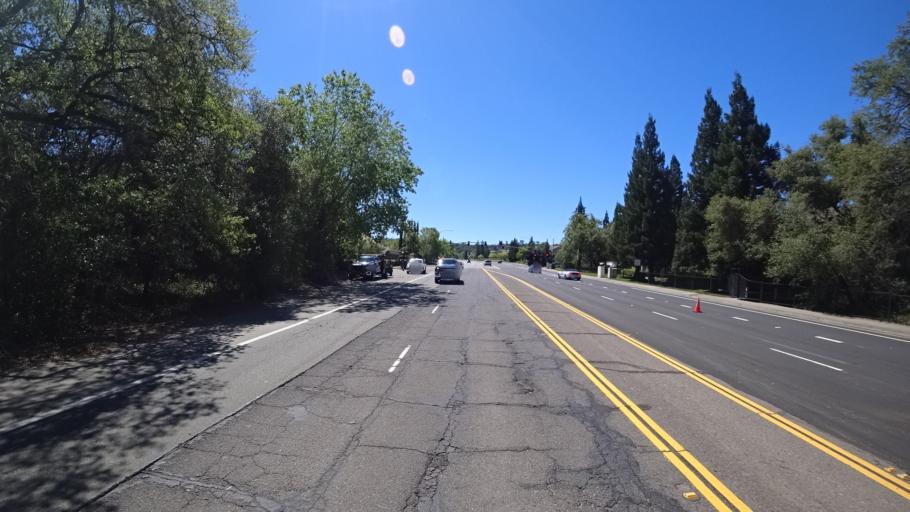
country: US
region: California
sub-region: Placer County
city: Rocklin
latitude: 38.7851
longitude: -121.2057
